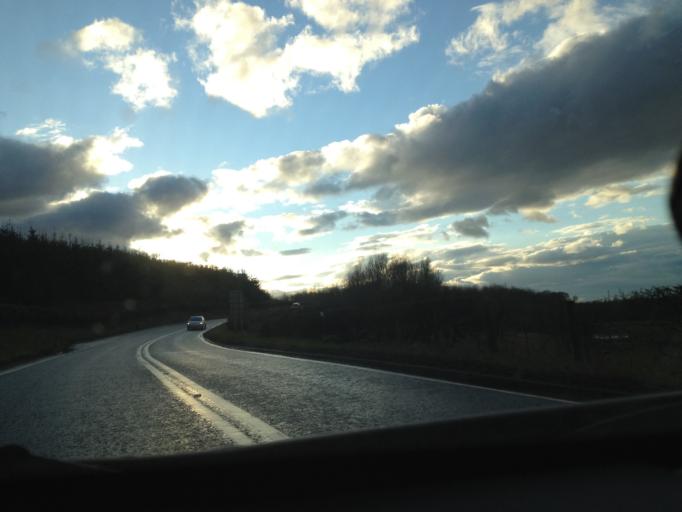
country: GB
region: Scotland
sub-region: South Lanarkshire
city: Larkhall
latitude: 55.7527
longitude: -3.9555
